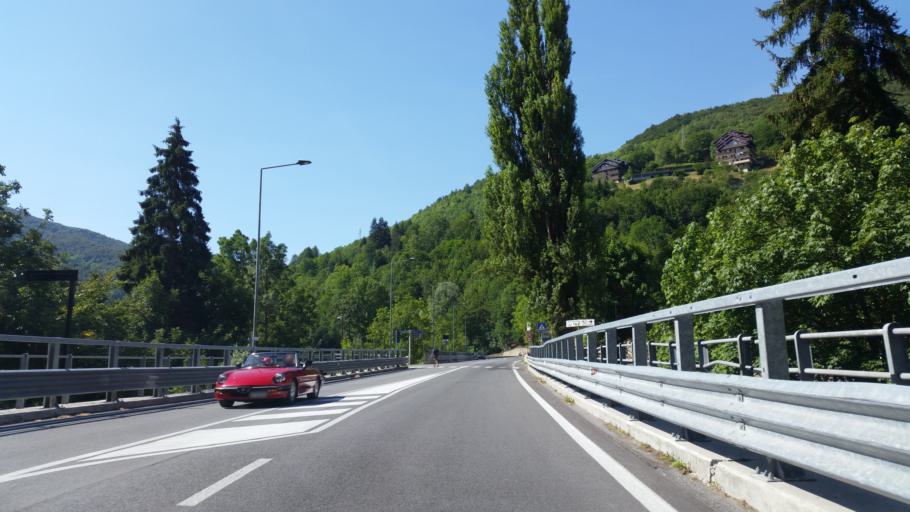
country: IT
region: Piedmont
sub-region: Provincia di Cuneo
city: Limone Piemonte
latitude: 44.2050
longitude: 7.5749
